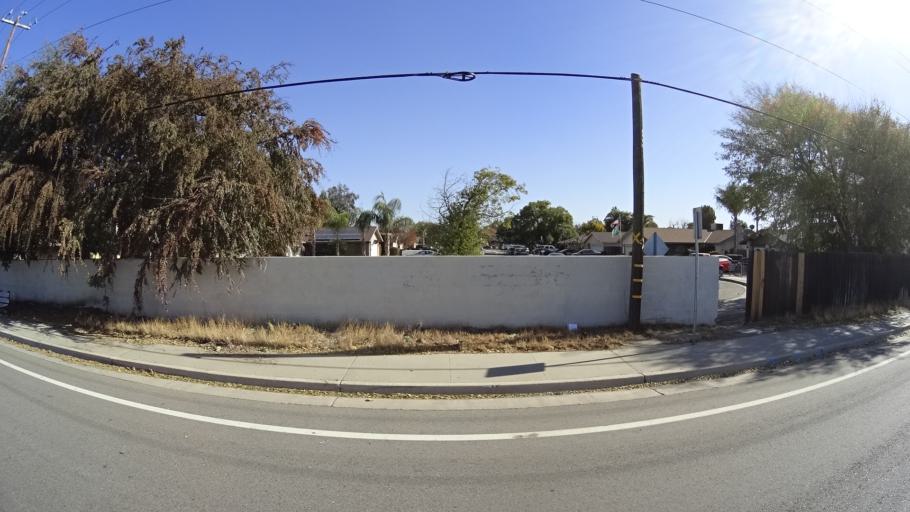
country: US
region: California
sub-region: Kern County
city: Greenfield
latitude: 35.3085
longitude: -119.0566
